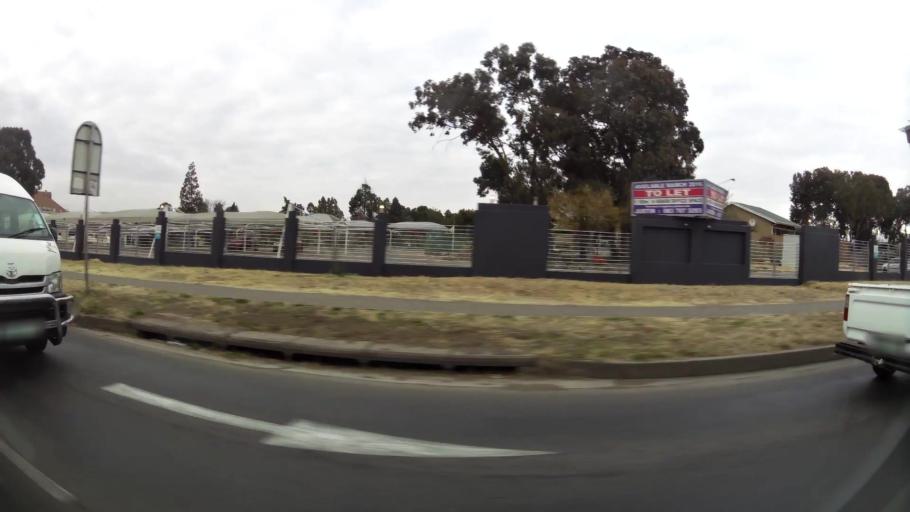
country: ZA
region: Orange Free State
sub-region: Mangaung Metropolitan Municipality
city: Bloemfontein
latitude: -29.1083
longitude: 26.1972
